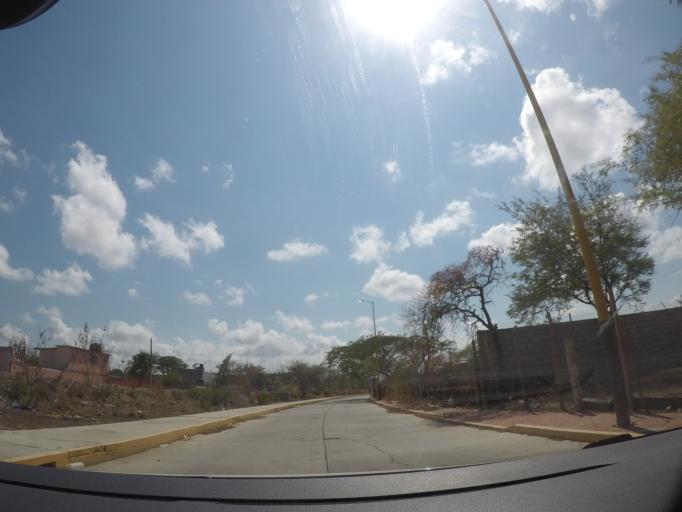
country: MX
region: Oaxaca
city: Juchitan de Zaragoza
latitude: 16.4352
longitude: -95.0113
